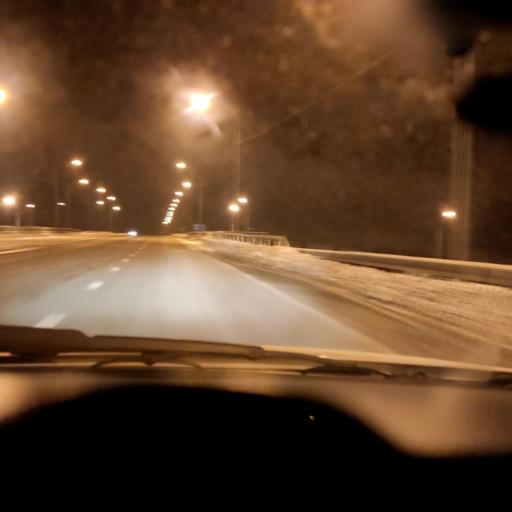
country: RU
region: Kursk
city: Fatezh
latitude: 52.0982
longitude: 35.8226
